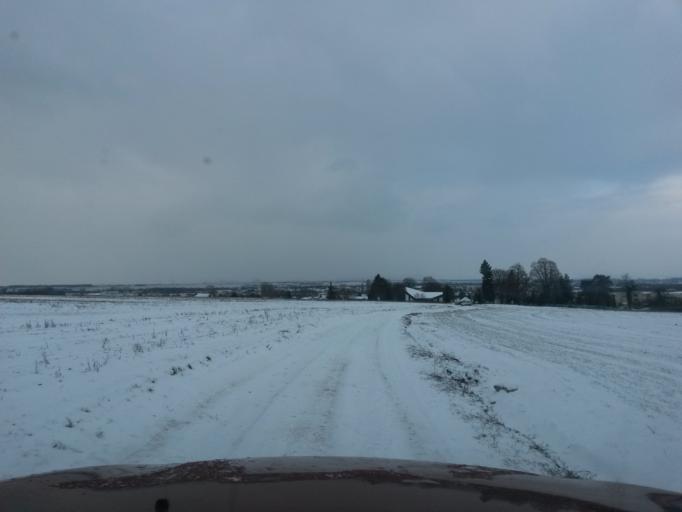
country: SK
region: Kosicky
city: Kosice
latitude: 48.6022
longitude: 21.3565
